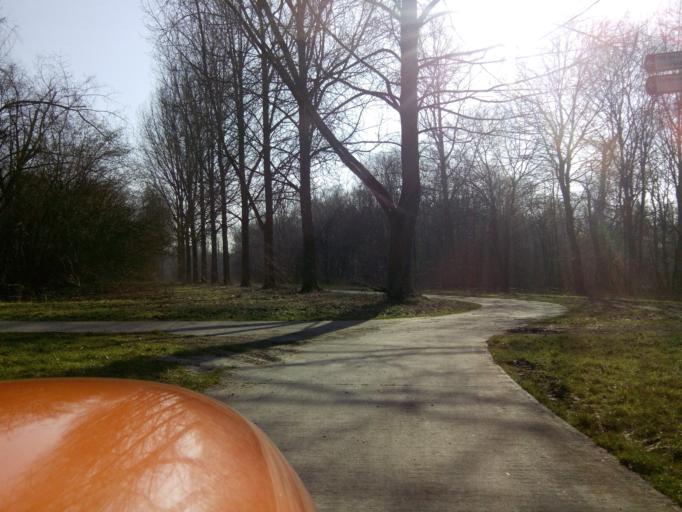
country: NL
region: Flevoland
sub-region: Gemeente Zeewolde
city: Zeewolde
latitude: 52.3036
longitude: 5.5007
